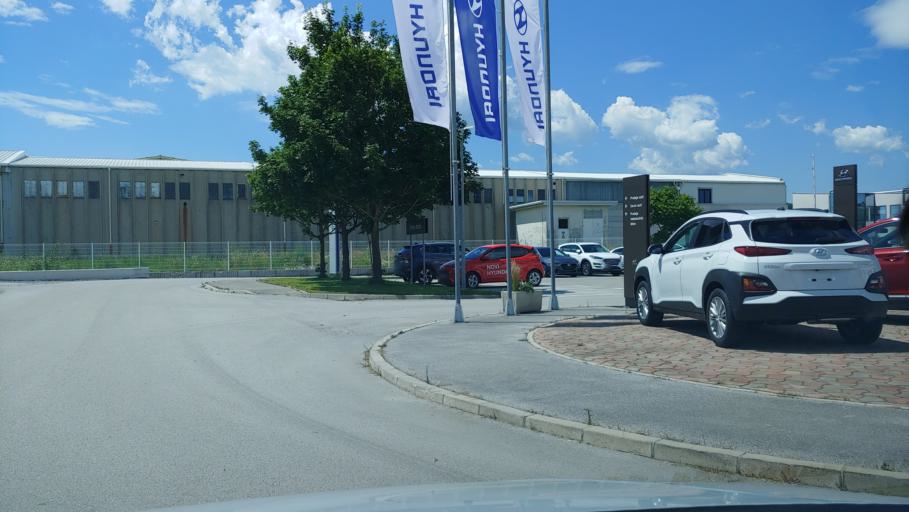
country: SI
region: Sezana
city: Sezana
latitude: 45.7032
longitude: 13.8547
